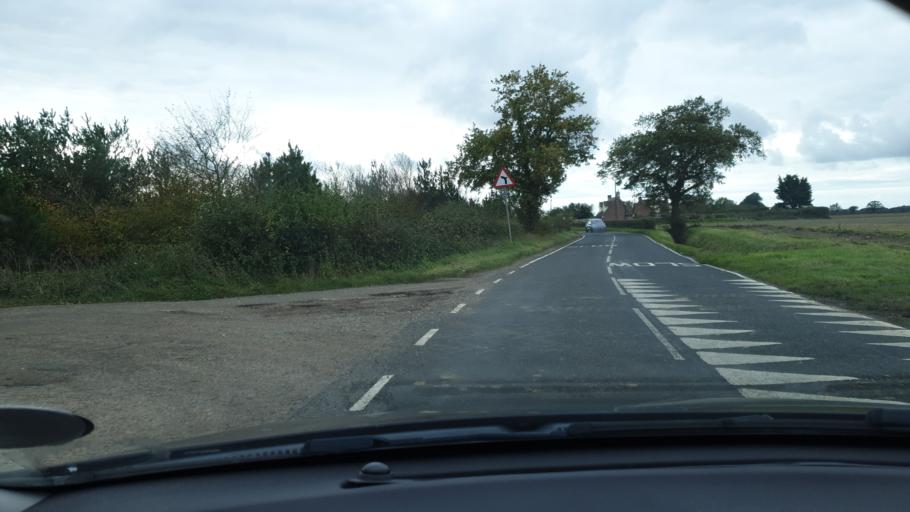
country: GB
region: England
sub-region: Essex
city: Manningtree
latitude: 51.9137
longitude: 1.0512
